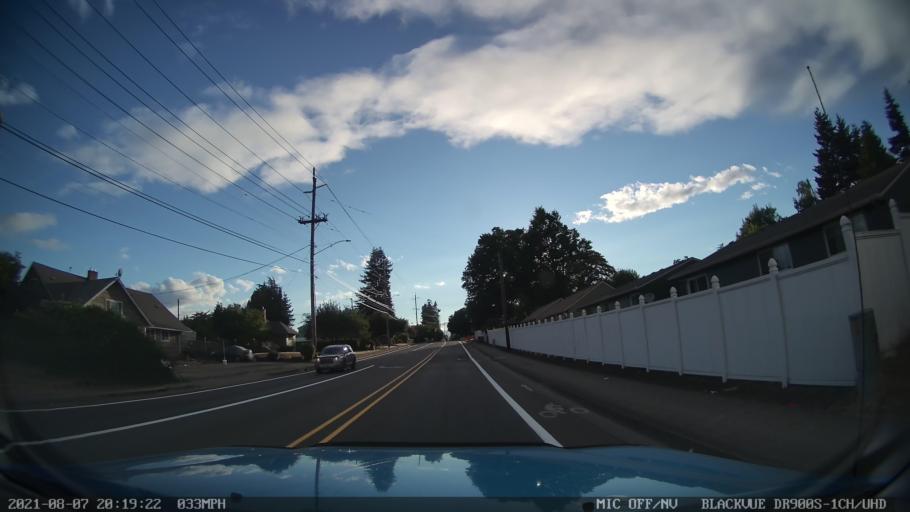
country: US
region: Oregon
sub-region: Marion County
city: Four Corners
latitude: 44.9540
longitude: -122.9920
